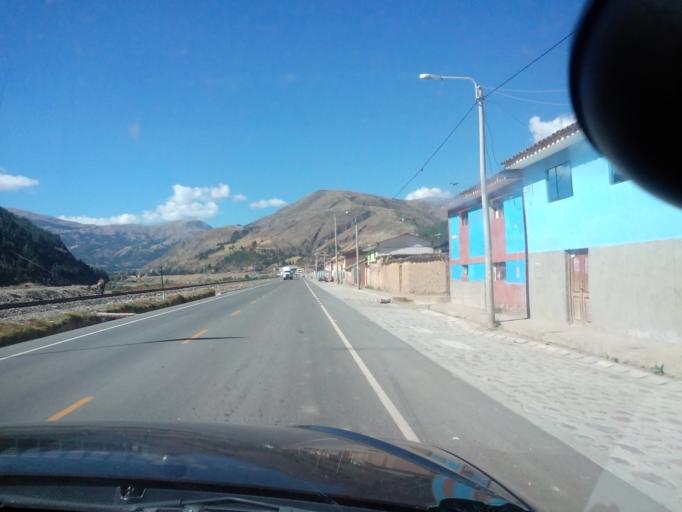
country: PE
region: Cusco
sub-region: Provincia de Quispicanchis
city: Urcos
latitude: -13.6760
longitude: -71.6295
